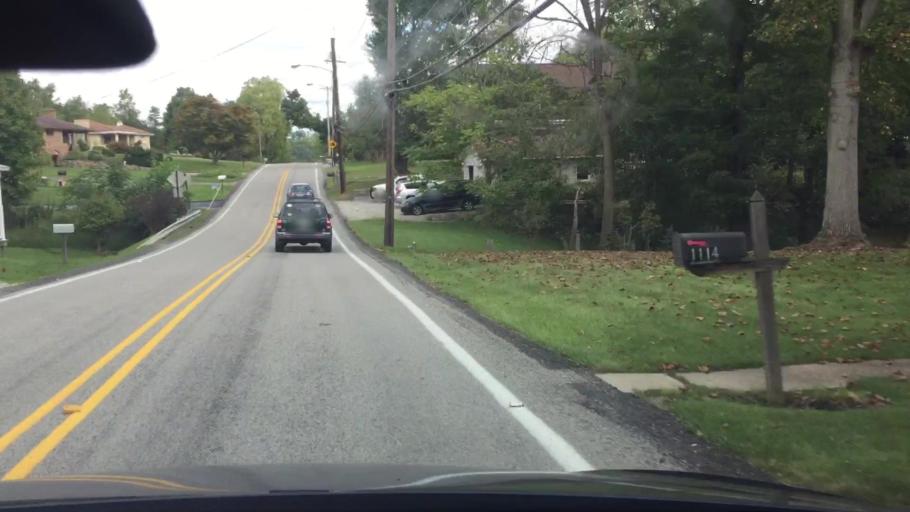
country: US
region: Pennsylvania
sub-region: Allegheny County
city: Cheswick
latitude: 40.5004
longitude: -79.7965
